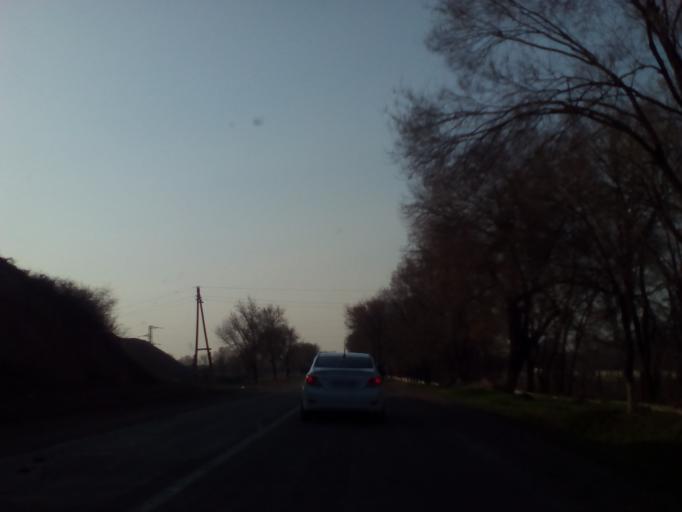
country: KZ
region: Almaty Oblysy
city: Burunday
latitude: 43.1717
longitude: 76.5312
